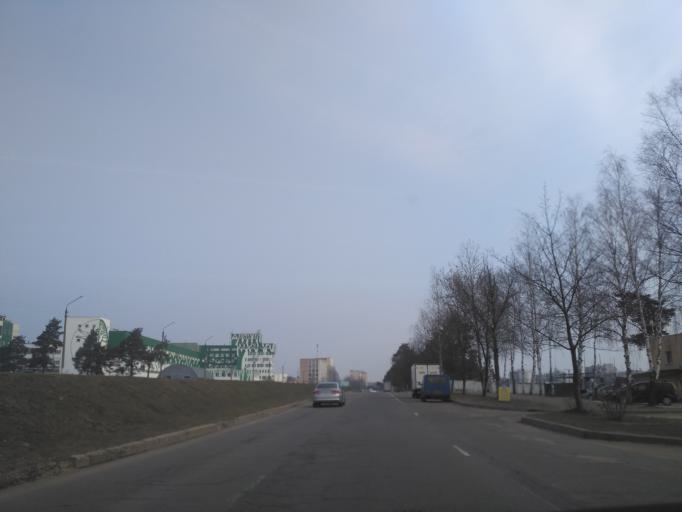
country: BY
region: Minsk
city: Horad Barysaw
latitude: 54.2031
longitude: 28.4985
